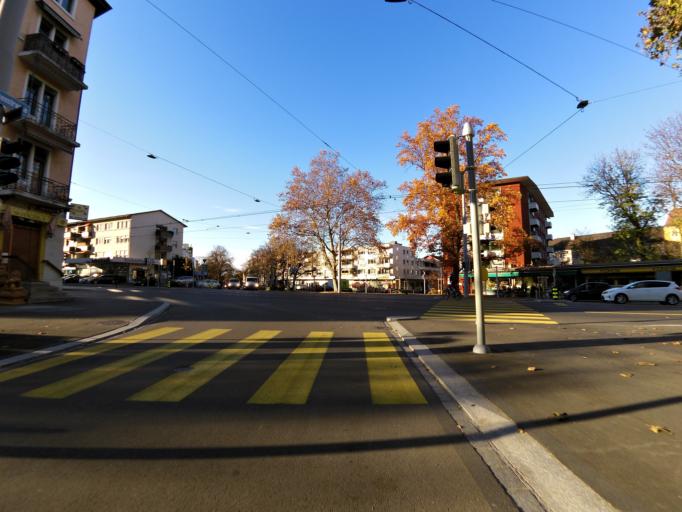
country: CH
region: Zurich
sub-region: Bezirk Zuerich
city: Zuerich (Kreis 3) / Sihlfeld
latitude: 47.3697
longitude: 8.5104
